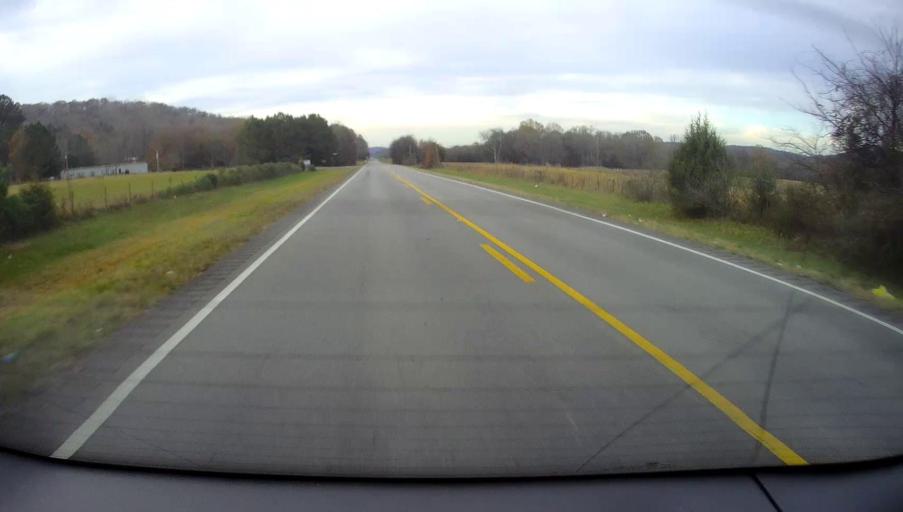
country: US
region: Alabama
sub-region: Marshall County
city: Arab
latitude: 34.3951
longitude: -86.6759
